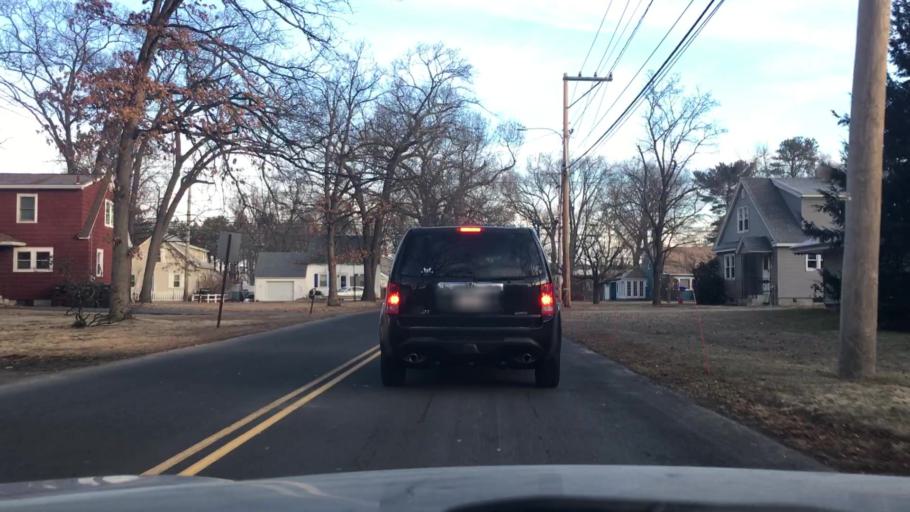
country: US
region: Massachusetts
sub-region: Hampden County
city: Westfield
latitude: 42.1378
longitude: -72.7272
